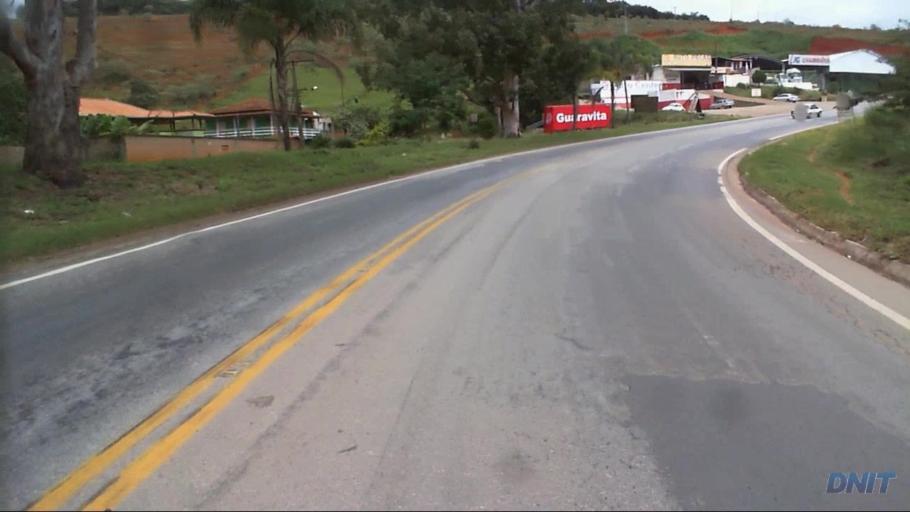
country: BR
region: Minas Gerais
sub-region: Joao Monlevade
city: Joao Monlevade
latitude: -19.8394
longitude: -43.1913
